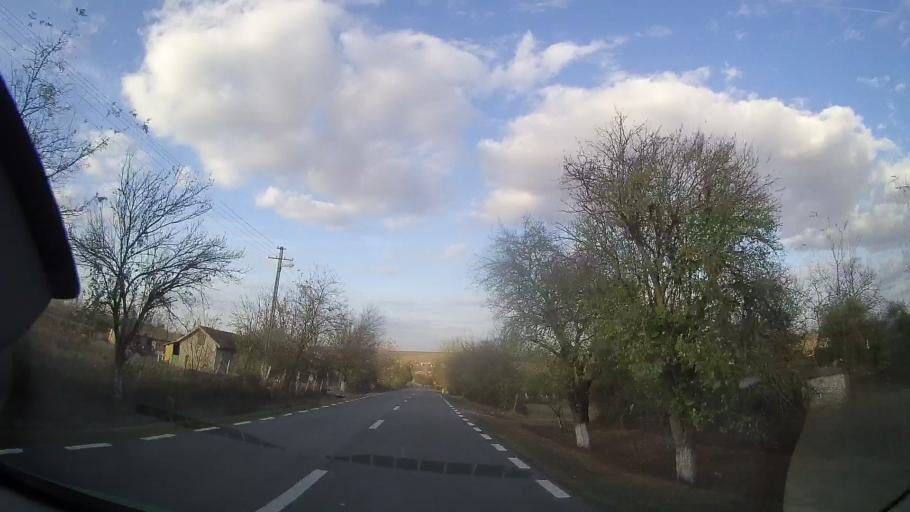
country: RO
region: Constanta
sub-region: Comuna Independenta
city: Independenta
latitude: 43.9514
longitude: 28.0750
